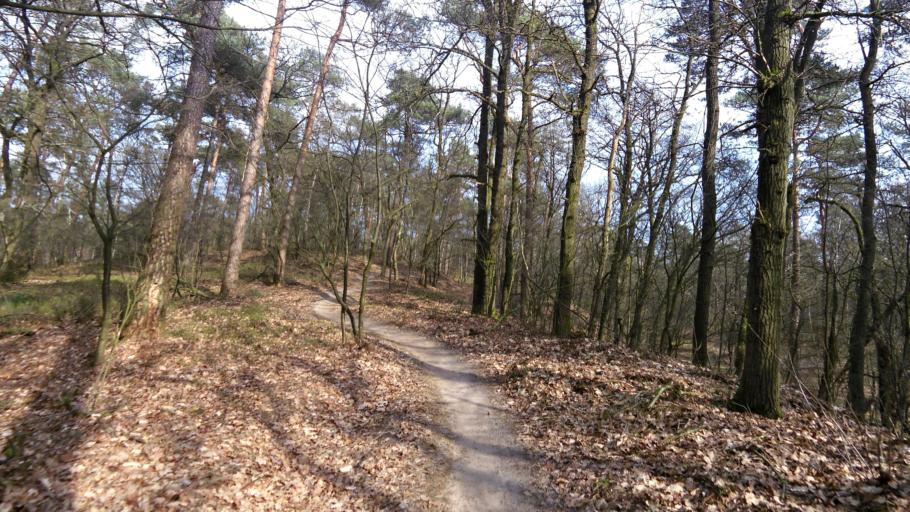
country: NL
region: Gelderland
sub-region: Gemeente Ede
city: Otterlo
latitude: 52.0803
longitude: 5.7417
